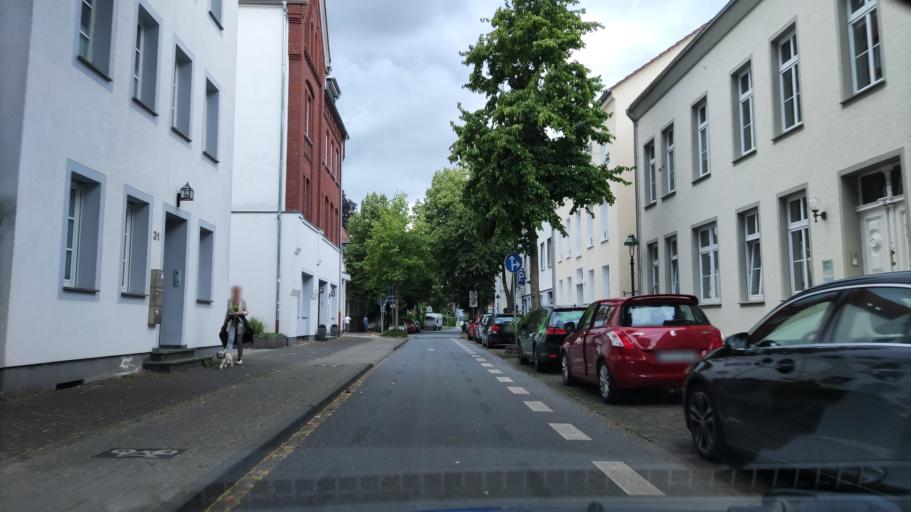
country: DE
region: North Rhine-Westphalia
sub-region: Regierungsbezirk Arnsberg
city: Soest
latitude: 51.5725
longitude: 8.1014
